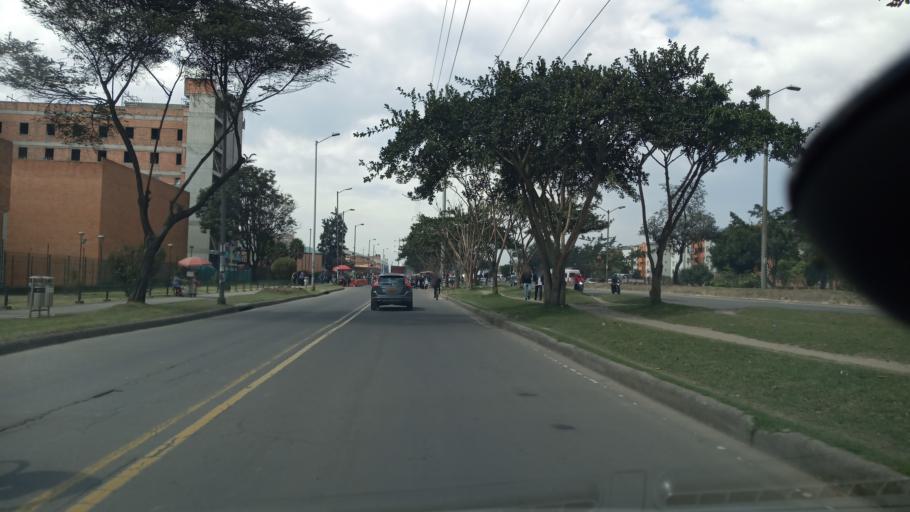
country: CO
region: Cundinamarca
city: Funza
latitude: 4.6749
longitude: -74.1533
